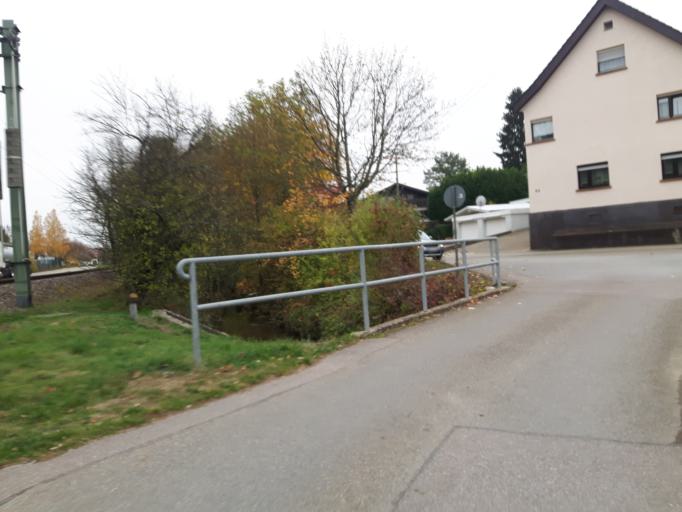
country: DE
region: Baden-Wuerttemberg
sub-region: Karlsruhe Region
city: Ostringen
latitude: 49.1801
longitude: 8.7417
